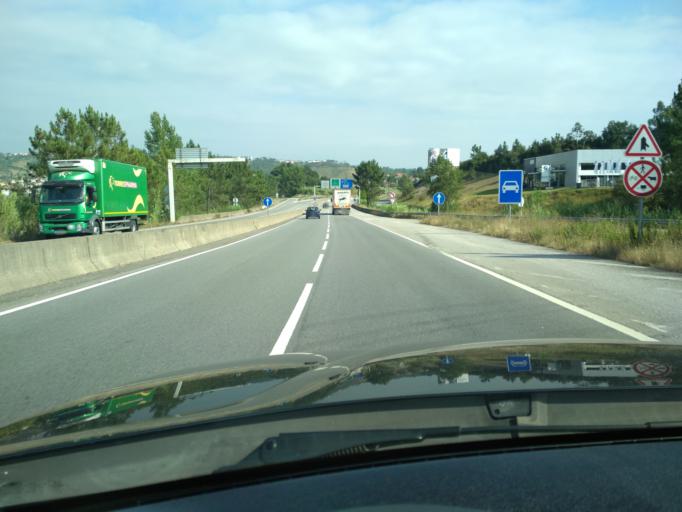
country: PT
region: Aveiro
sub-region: Mealhada
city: Pampilhosa do Botao
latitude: 40.2769
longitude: -8.4452
